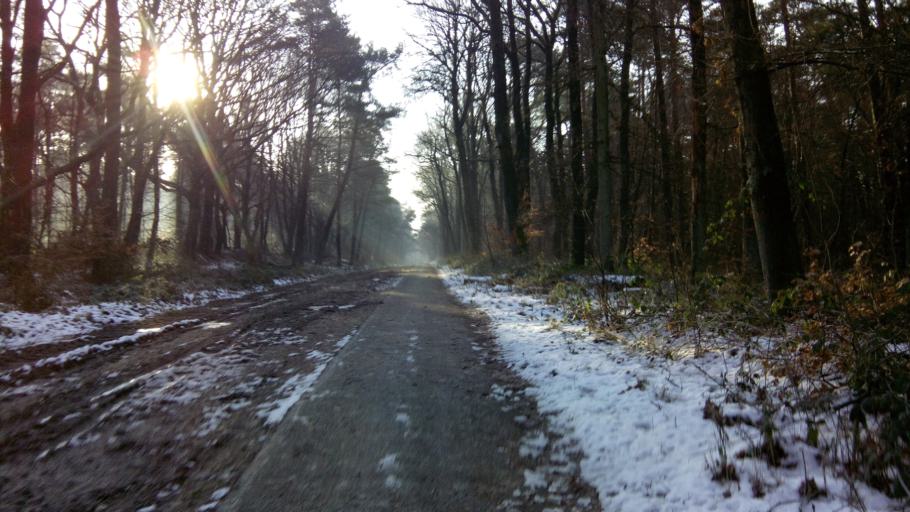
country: NL
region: Gelderland
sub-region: Gemeente Groesbeek
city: Berg en Dal
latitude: 51.8060
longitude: 5.8800
